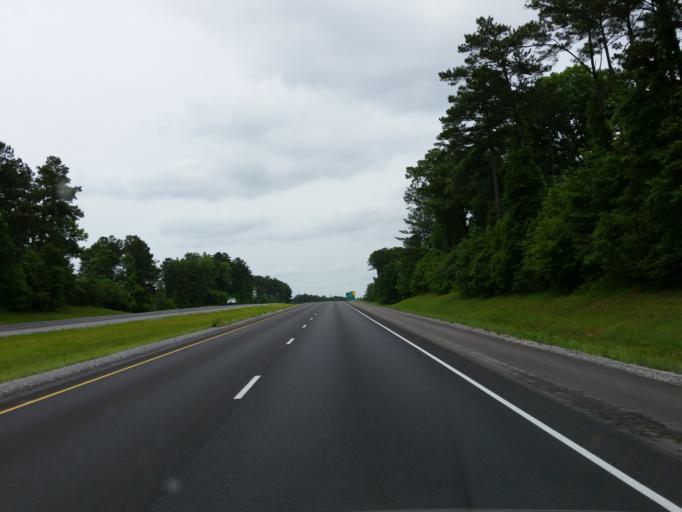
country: US
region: Mississippi
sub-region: Jones County
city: Sharon
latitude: 31.8940
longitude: -89.0313
